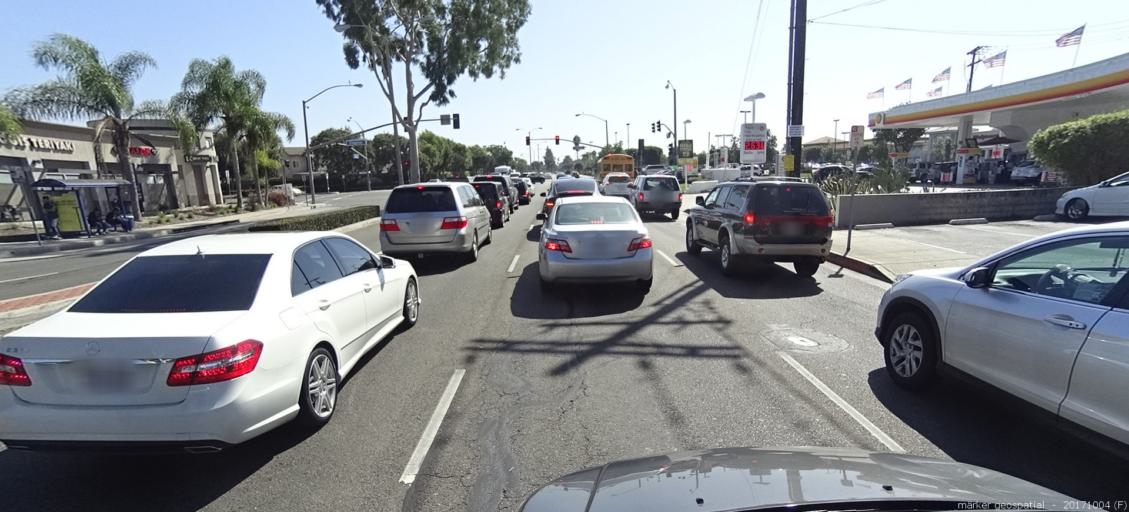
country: US
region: California
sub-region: Orange County
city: Garden Grove
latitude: 33.7893
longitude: -117.9413
